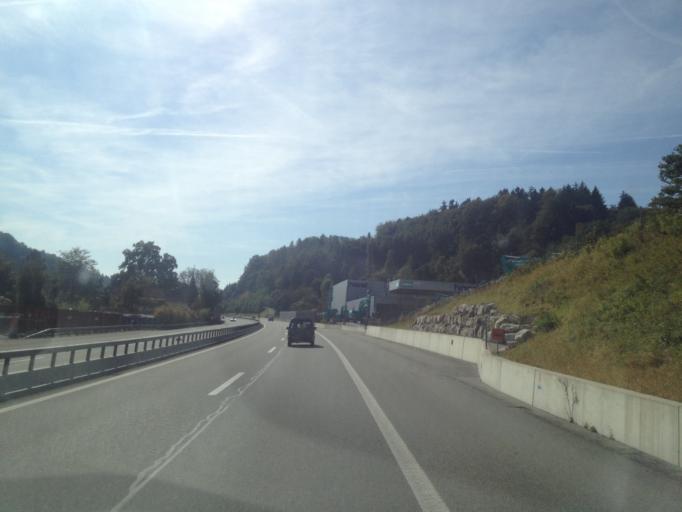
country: CH
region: Fribourg
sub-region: Sense District
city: Flamatt
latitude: 46.9073
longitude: 7.3573
